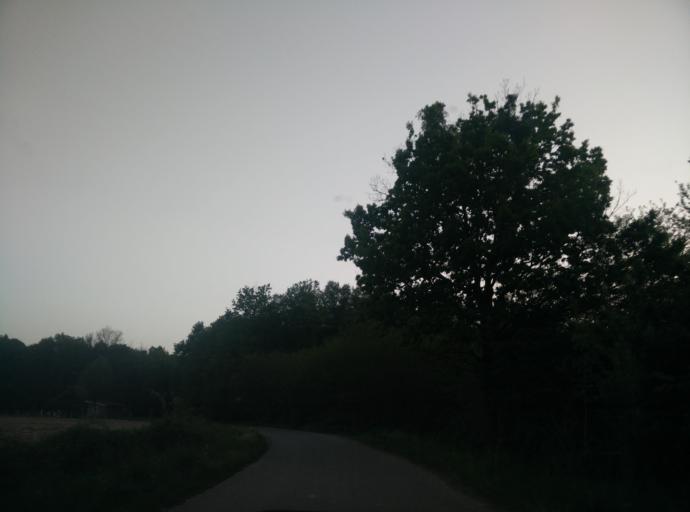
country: BA
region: Brcko
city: Brcko
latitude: 44.7772
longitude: 18.8437
